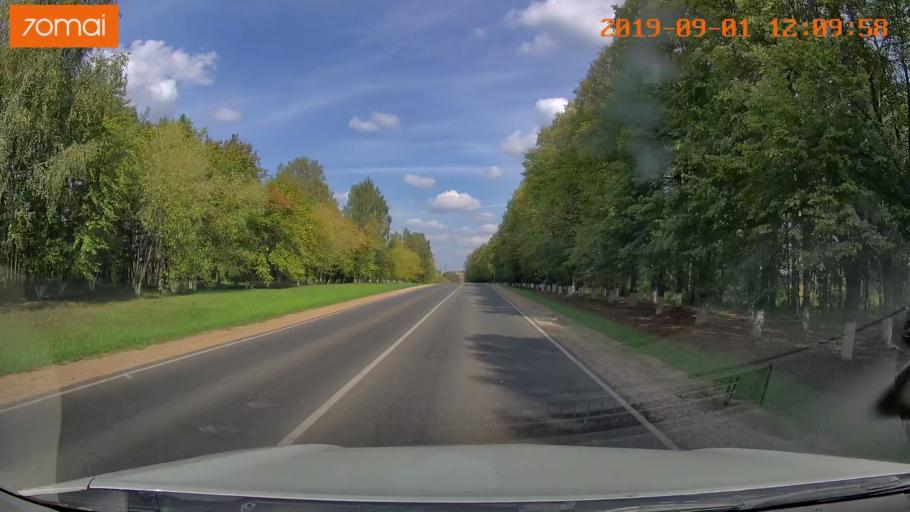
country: RU
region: Kaluga
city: Maloyaroslavets
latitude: 54.9863
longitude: 36.4296
